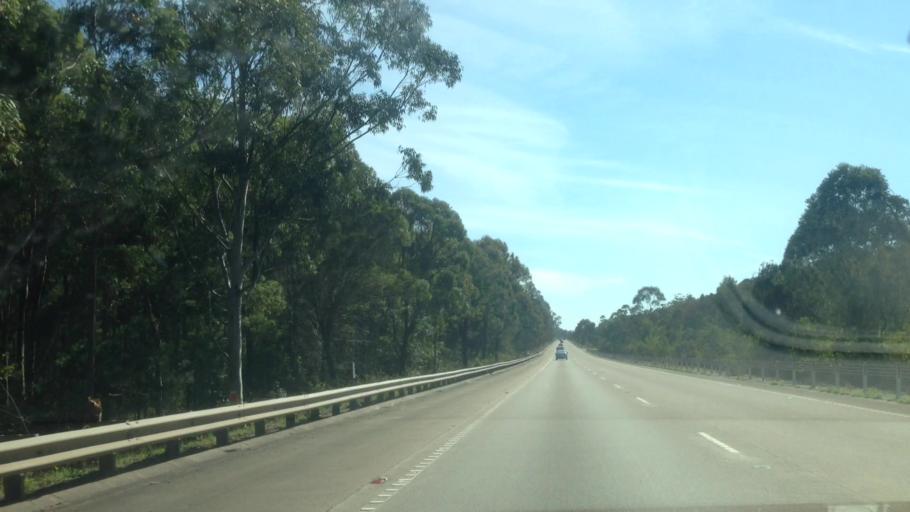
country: AU
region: New South Wales
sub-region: Lake Macquarie Shire
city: Fennell Bay
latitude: -32.9718
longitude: 151.5332
